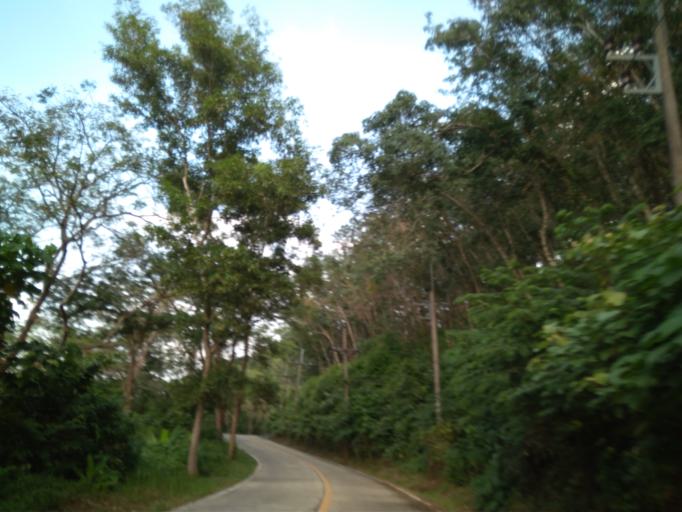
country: TH
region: Phangnga
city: Ko Yao
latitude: 8.1375
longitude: 98.6152
